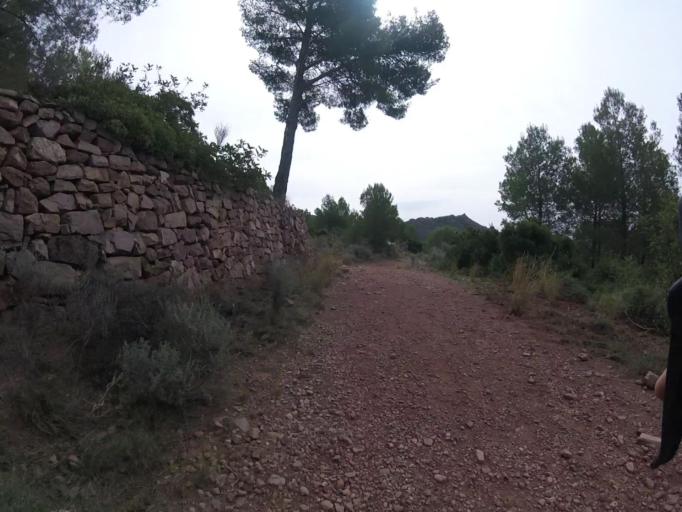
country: ES
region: Valencia
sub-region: Provincia de Castello
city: Benicassim
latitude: 40.0768
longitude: 0.0355
